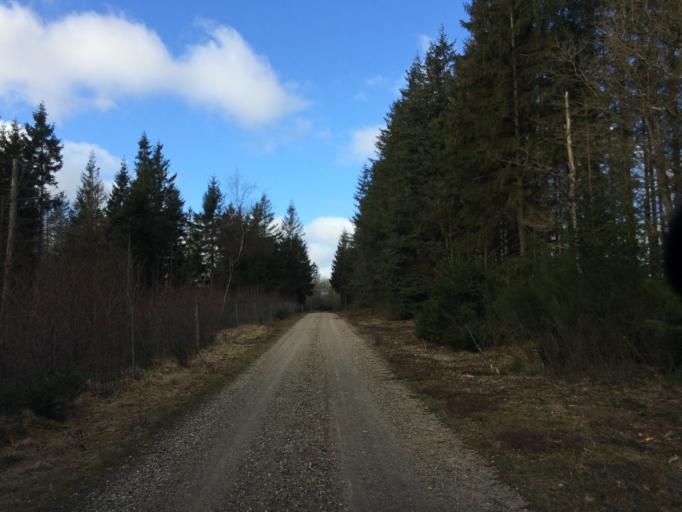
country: DK
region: Central Jutland
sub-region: Holstebro Kommune
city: Ulfborg
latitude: 56.2725
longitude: 8.4422
